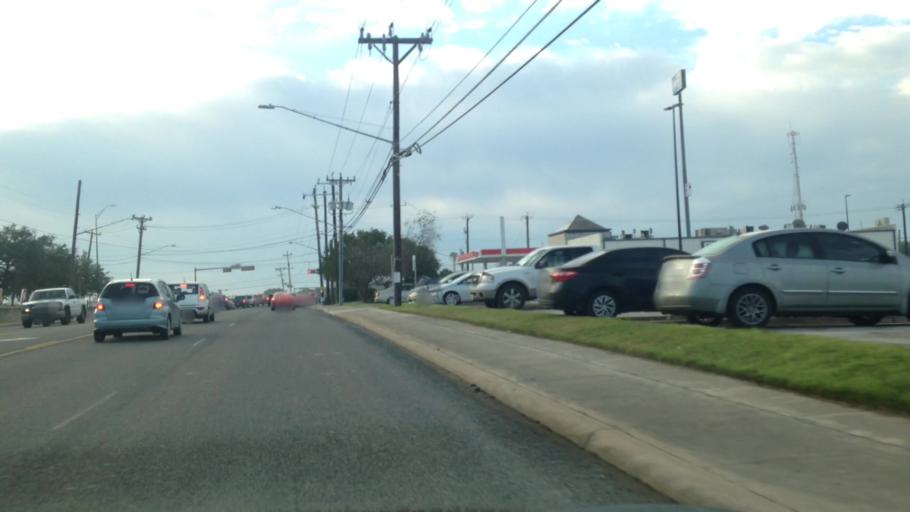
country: US
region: Texas
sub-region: Bexar County
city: Live Oak
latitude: 29.5538
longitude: -98.3565
